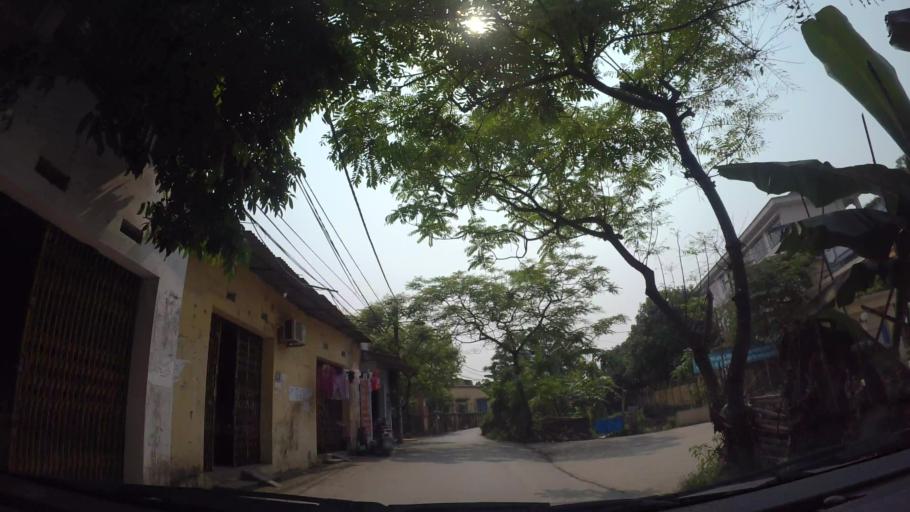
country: VN
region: Ha Noi
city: Ha Dong
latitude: 21.0012
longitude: 105.7567
